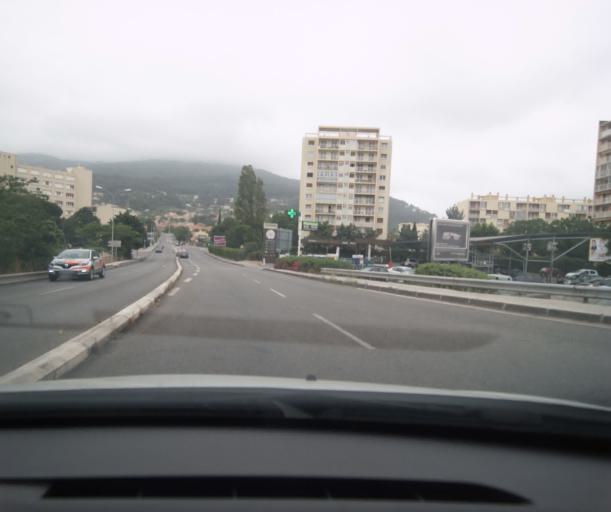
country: FR
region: Provence-Alpes-Cote d'Azur
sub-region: Departement du Var
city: La Valette-du-Var
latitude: 43.1334
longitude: 5.9815
